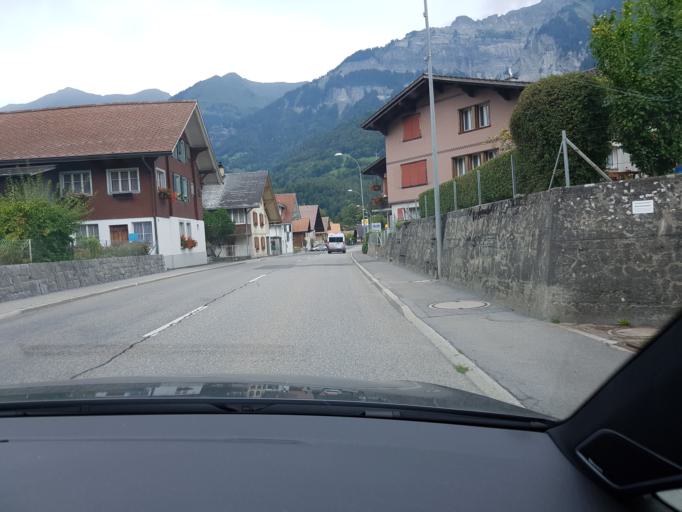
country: CH
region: Bern
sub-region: Interlaken-Oberhasli District
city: Brienz
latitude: 46.7483
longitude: 8.0541
